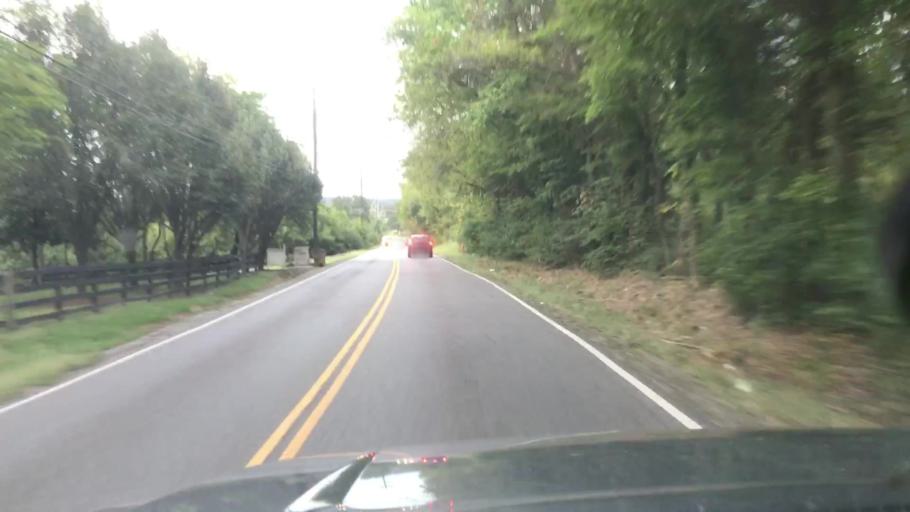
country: US
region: Tennessee
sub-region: Rutherford County
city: La Vergne
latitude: 36.0520
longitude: -86.6219
